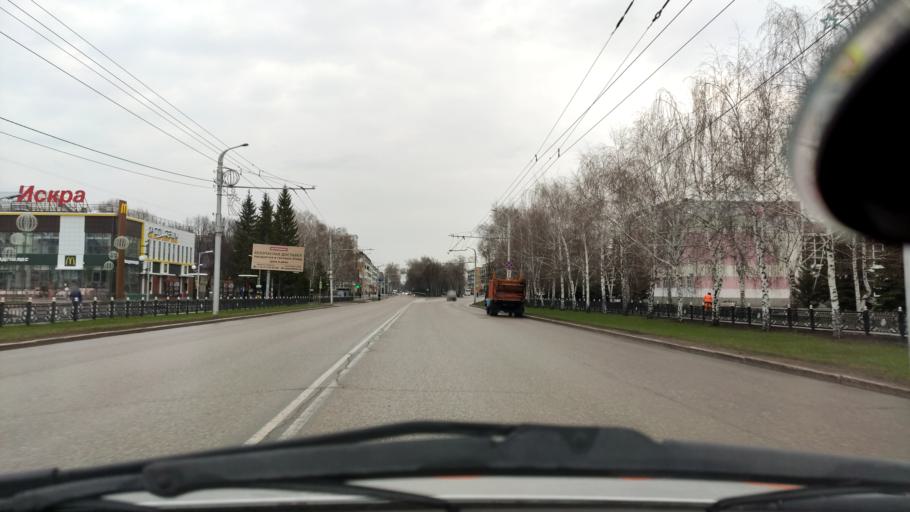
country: RU
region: Bashkortostan
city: Sterlitamak
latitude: 53.6367
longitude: 55.9362
